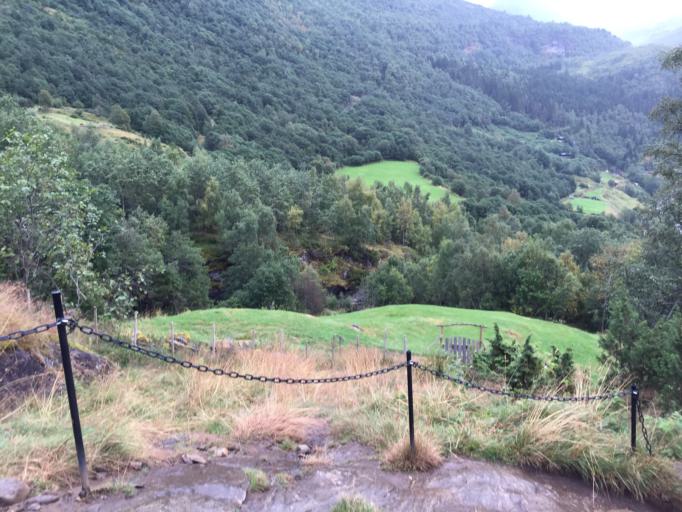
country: NO
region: More og Romsdal
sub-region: Norddal
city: Valldal
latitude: 62.1008
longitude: 7.2236
